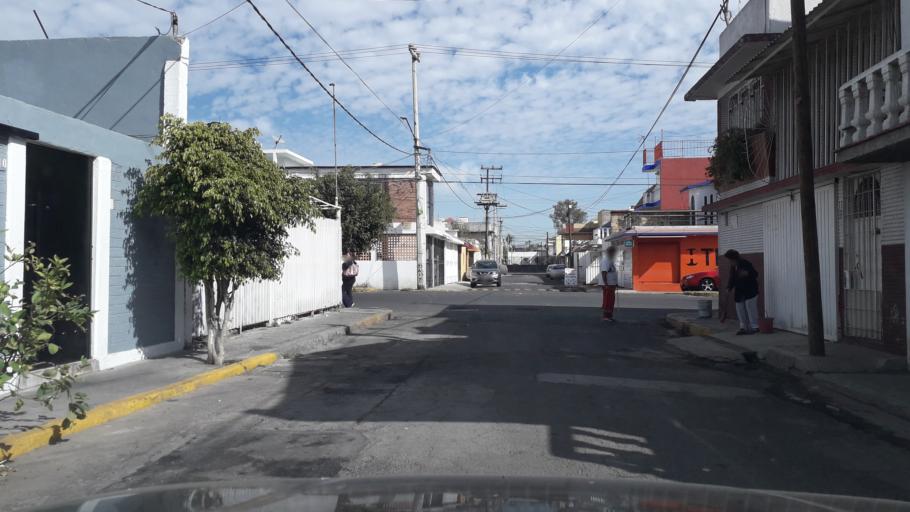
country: MX
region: Mexico City
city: Gustavo A. Madero
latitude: 19.5093
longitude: -99.0877
